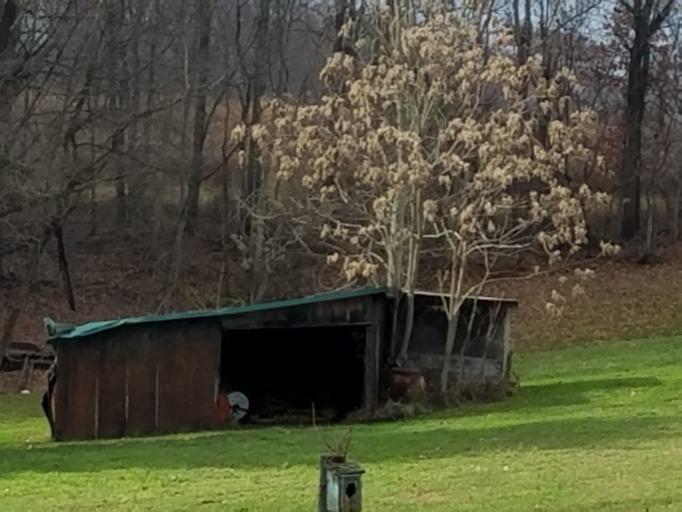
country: US
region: Ohio
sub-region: Sandusky County
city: Bellville
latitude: 40.5672
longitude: -82.3811
